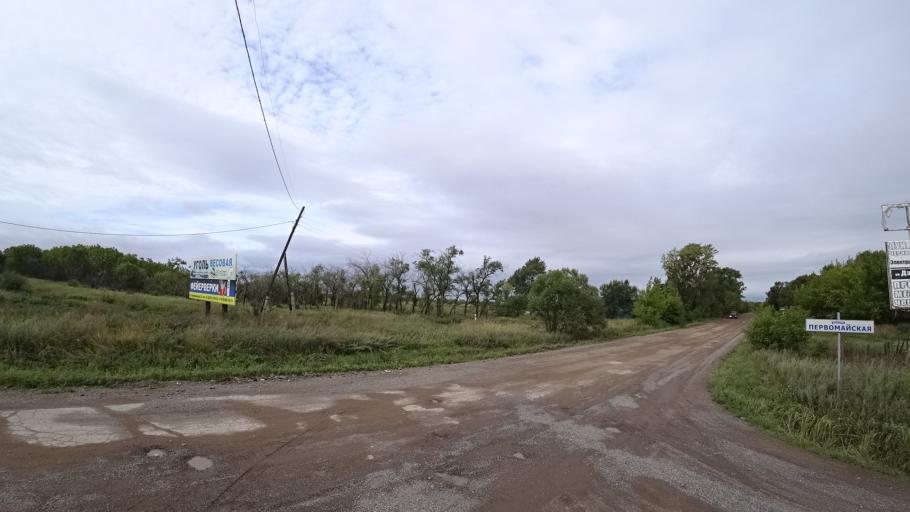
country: RU
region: Primorskiy
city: Chernigovka
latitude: 44.3285
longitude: 132.5729
